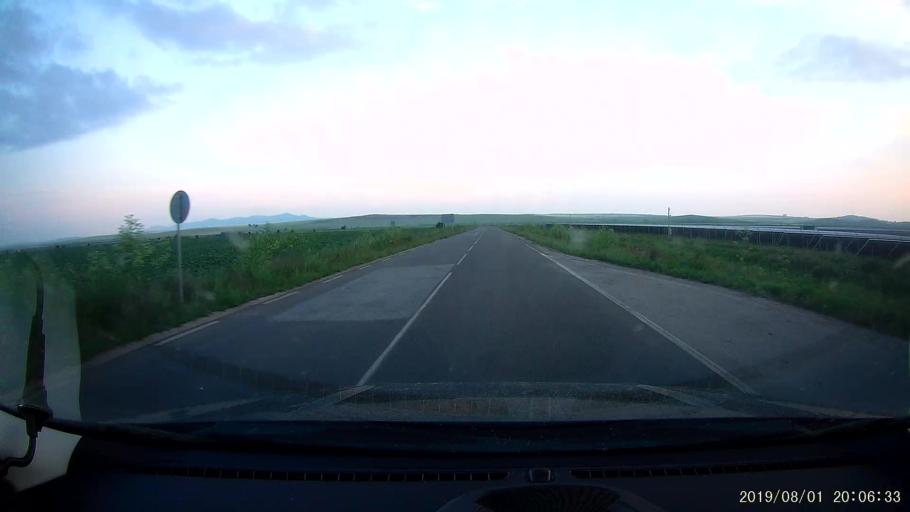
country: BG
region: Yambol
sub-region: Obshtina Yambol
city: Yambol
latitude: 42.5332
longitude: 26.5567
